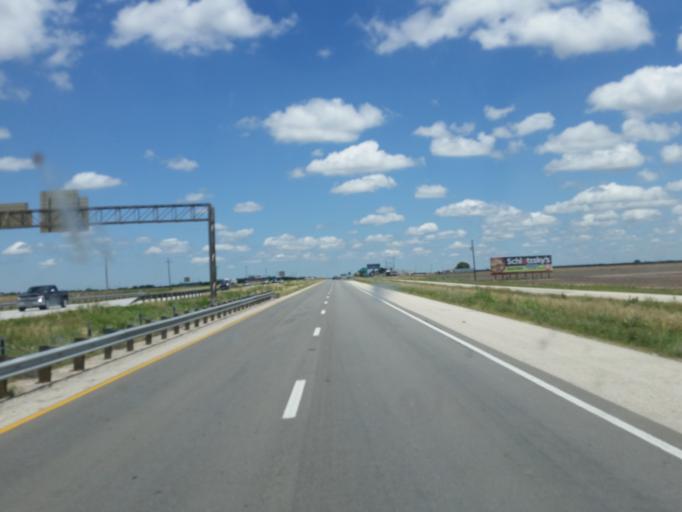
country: US
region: Texas
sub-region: Nolan County
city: Roscoe
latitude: 32.4483
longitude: -100.4944
